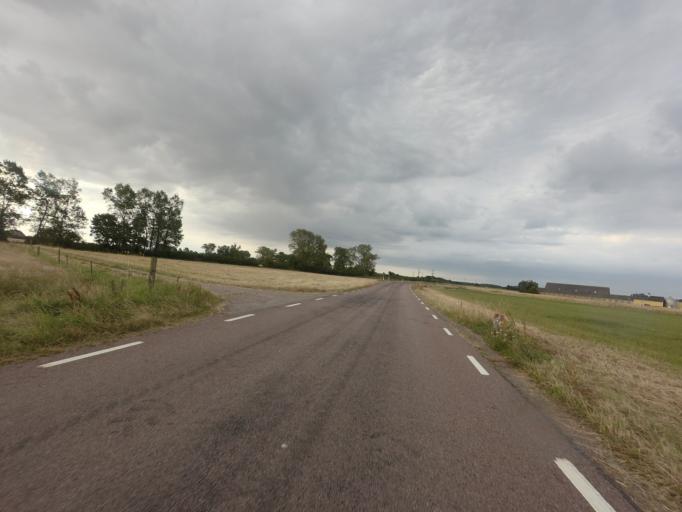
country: SE
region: Skane
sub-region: Helsingborg
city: Odakra
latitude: 56.1453
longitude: 12.7326
